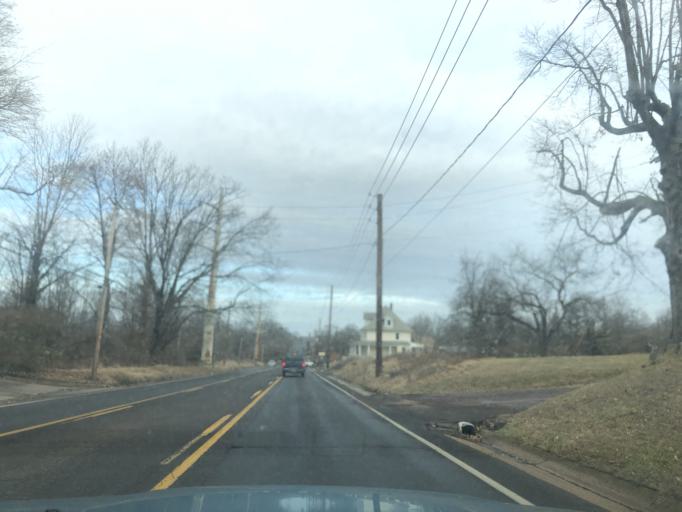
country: US
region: Pennsylvania
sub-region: Bucks County
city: Sellersville
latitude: 40.3322
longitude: -75.3033
